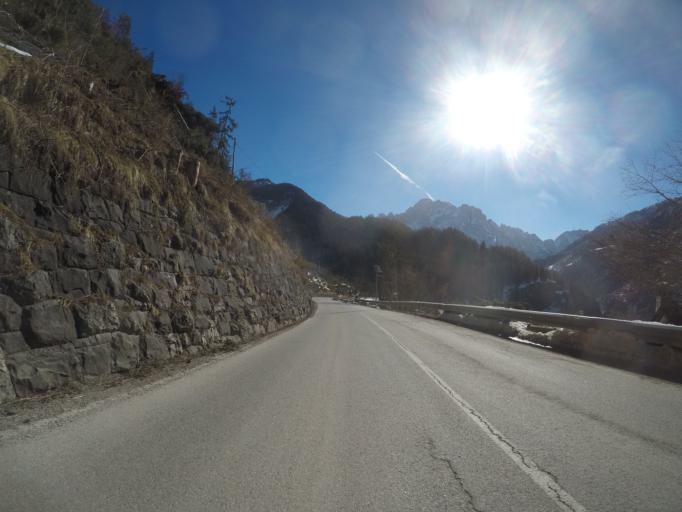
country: IT
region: Veneto
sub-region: Provincia di Belluno
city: Colle Santa Lucia
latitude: 46.4412
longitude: 11.9979
